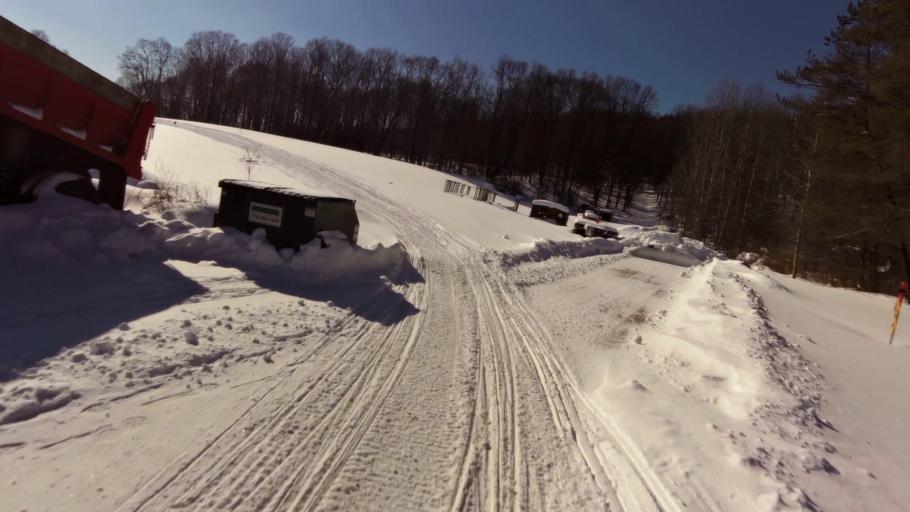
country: US
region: New York
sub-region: Cattaraugus County
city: Franklinville
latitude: 42.4034
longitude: -78.5023
